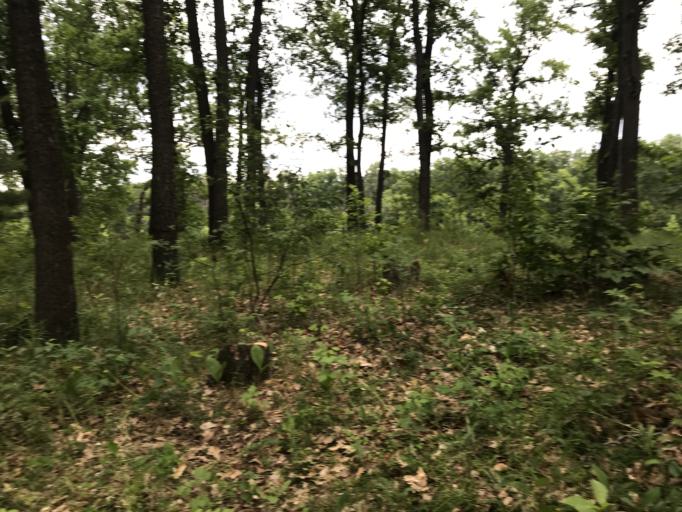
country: RU
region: Samara
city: Pribrezhnyy
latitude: 53.4683
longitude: 49.8164
